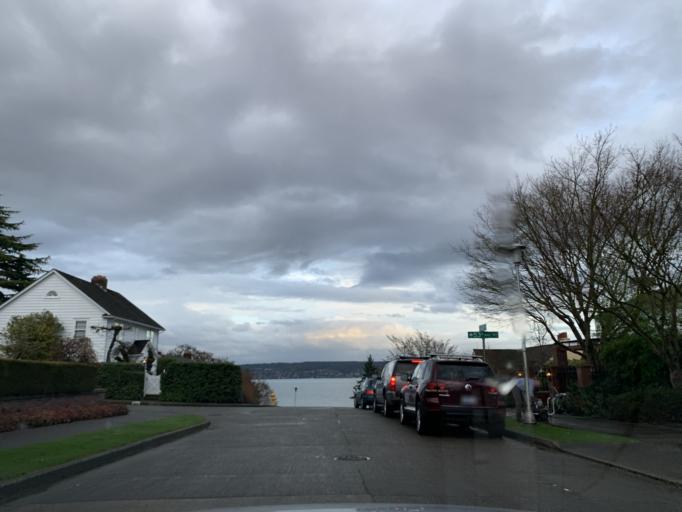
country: US
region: Washington
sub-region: King County
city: Yarrow Point
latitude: 47.6587
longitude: -122.2714
